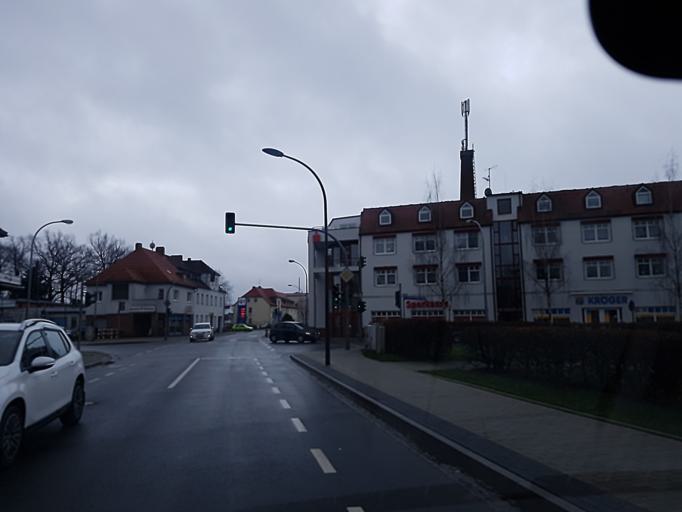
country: DE
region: Brandenburg
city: Finsterwalde
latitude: 51.6251
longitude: 13.7163
